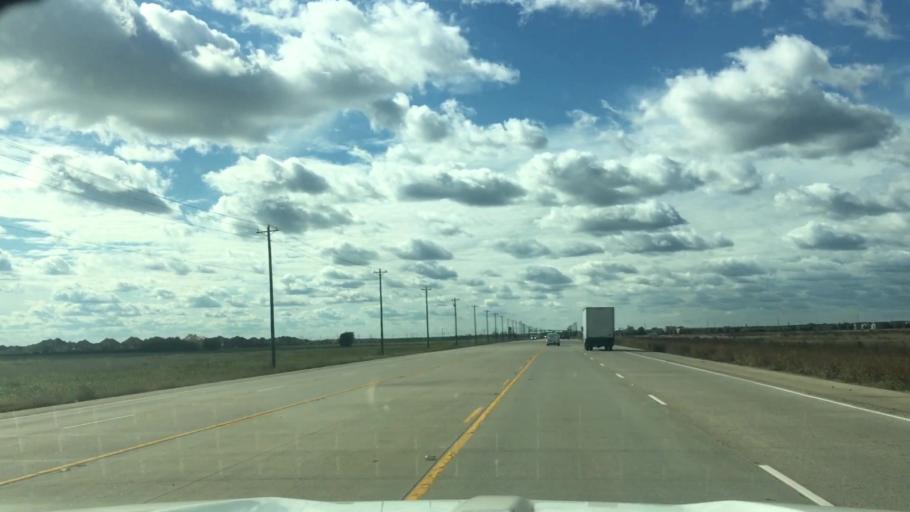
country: US
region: Texas
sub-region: Collin County
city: Prosper
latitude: 33.2192
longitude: -96.8642
